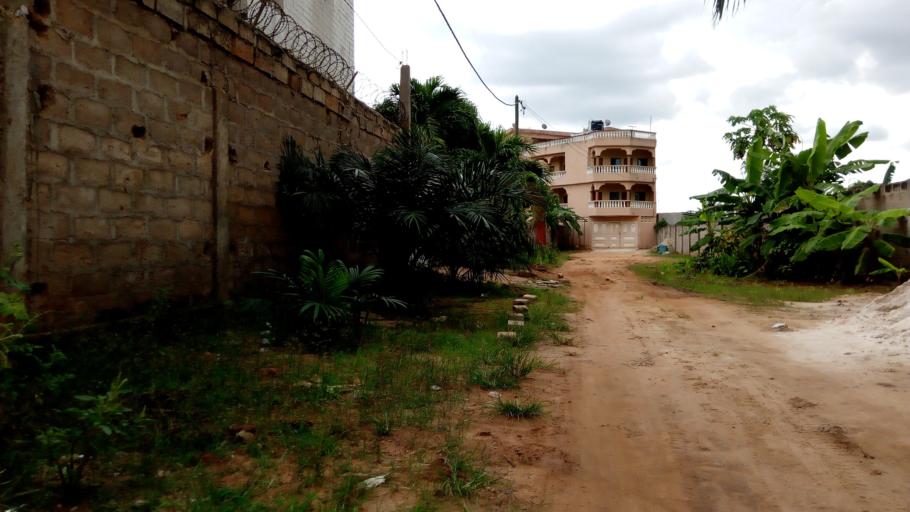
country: TG
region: Maritime
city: Lome
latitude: 6.1709
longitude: 1.1875
